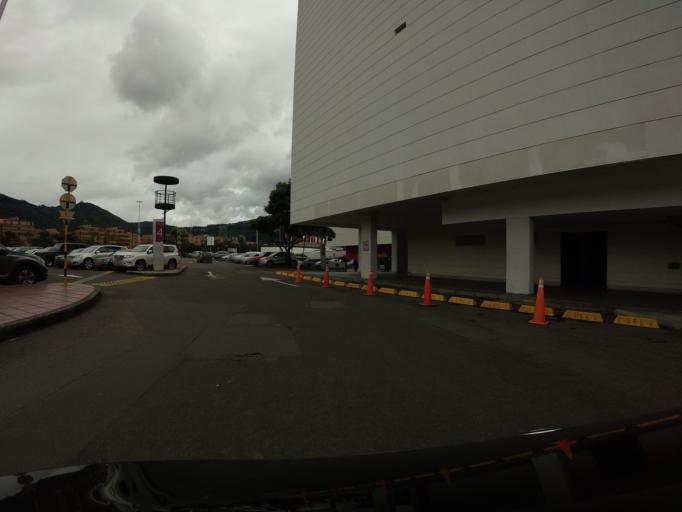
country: CO
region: Bogota D.C.
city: Barrio San Luis
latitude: 4.7032
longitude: -74.0409
